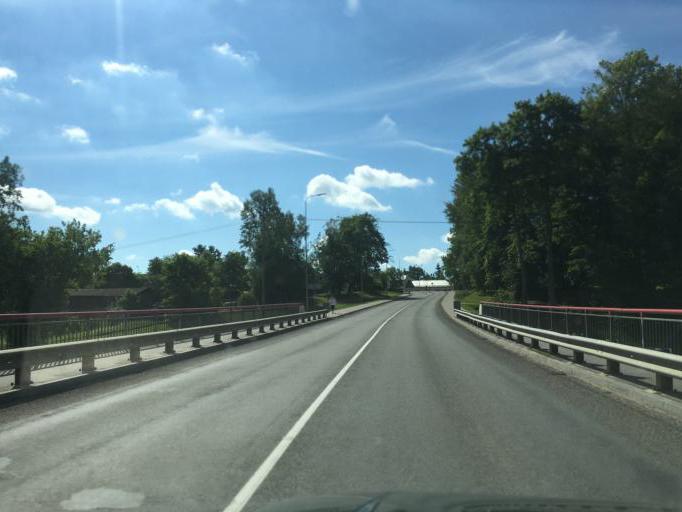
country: LV
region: Balvu Rajons
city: Balvi
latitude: 57.1347
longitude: 27.2613
